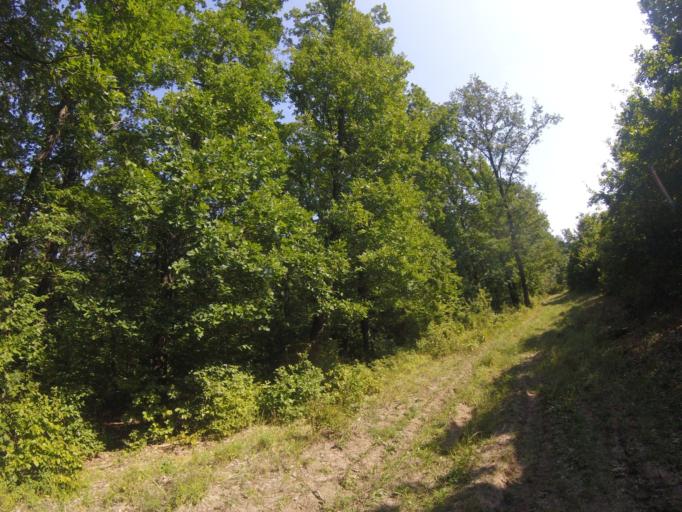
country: HU
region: Nograd
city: Bujak
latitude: 47.8975
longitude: 19.5116
